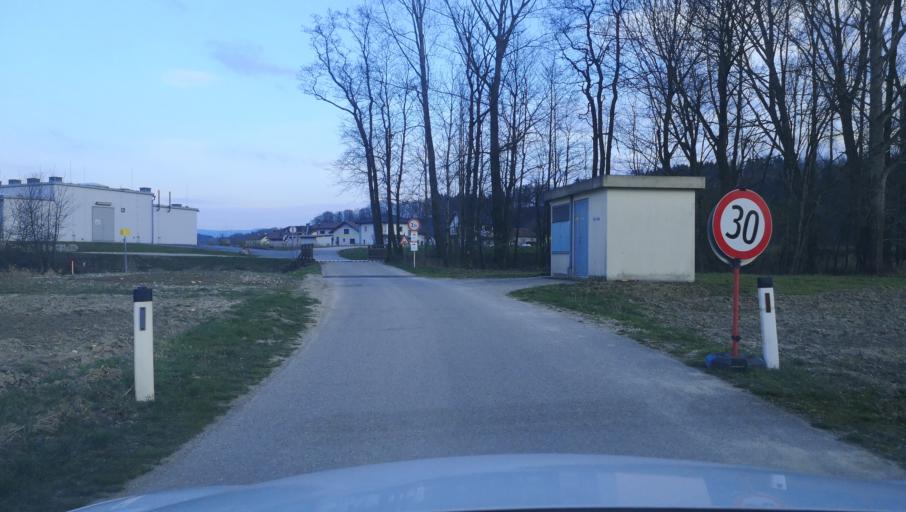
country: AT
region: Lower Austria
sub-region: Politischer Bezirk Amstetten
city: Euratsfeld
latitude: 48.1034
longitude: 14.9046
